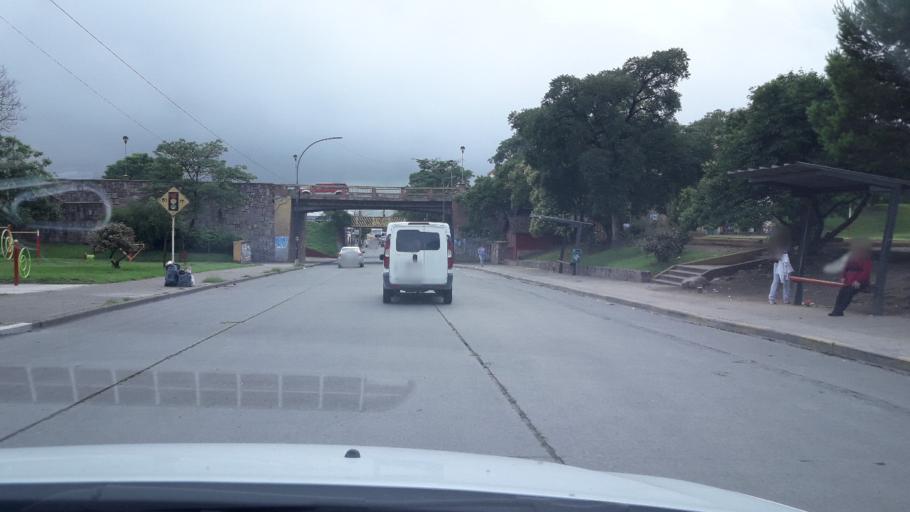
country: AR
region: Jujuy
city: San Salvador de Jujuy
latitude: -24.1920
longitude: -65.2940
